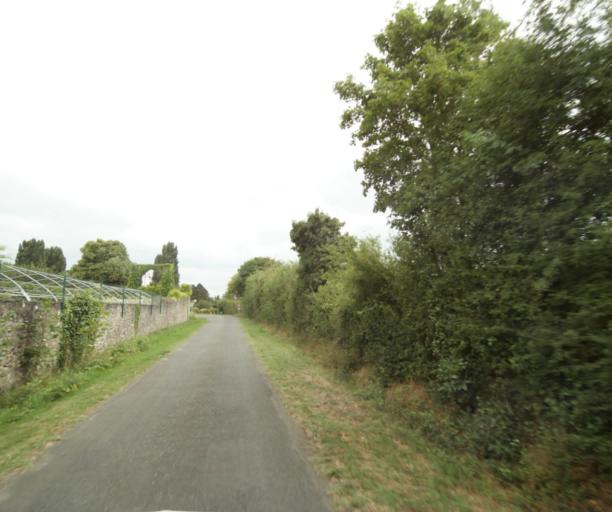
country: FR
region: Pays de la Loire
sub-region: Departement de la Sarthe
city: Solesmes
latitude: 47.8497
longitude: -0.3089
